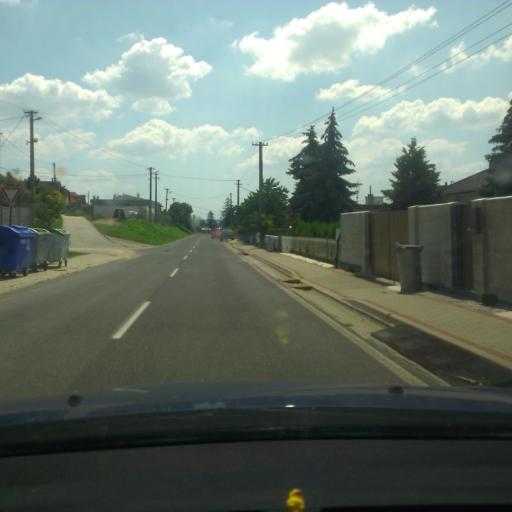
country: SK
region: Trnavsky
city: Hlohovec
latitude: 48.4791
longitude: 17.8078
